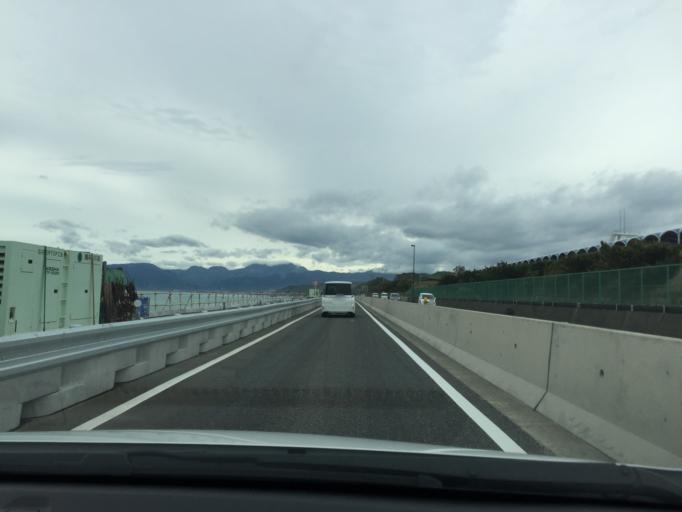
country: JP
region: Kanagawa
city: Oiso
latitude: 35.3002
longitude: 139.2818
